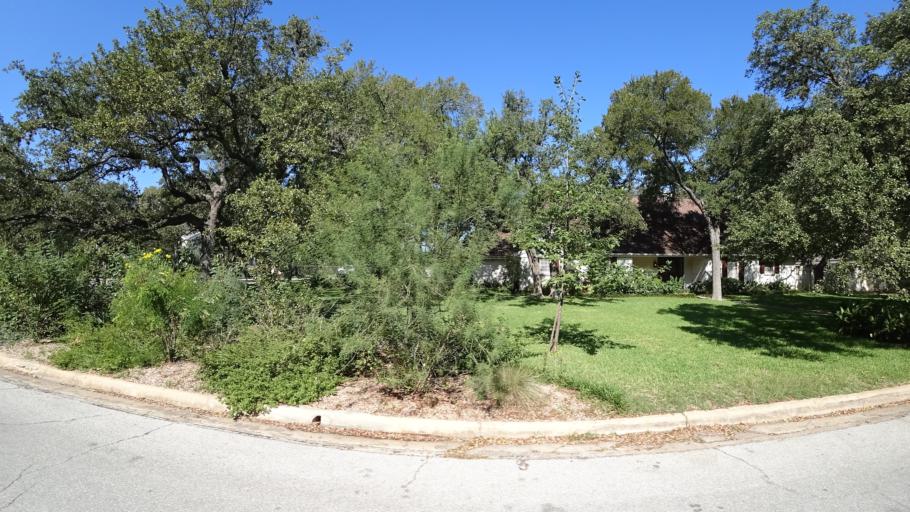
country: US
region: Texas
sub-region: Travis County
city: Rollingwood
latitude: 30.2732
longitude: -97.8110
